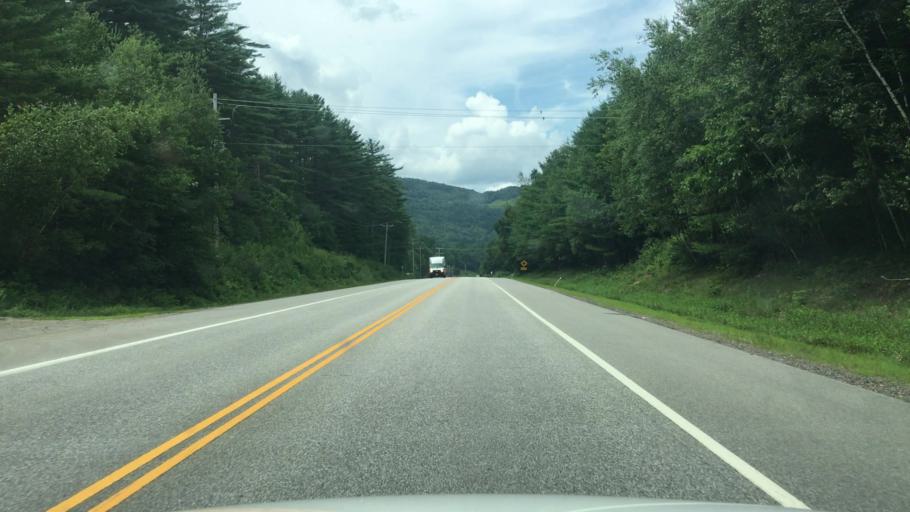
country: US
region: New Hampshire
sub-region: Grafton County
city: Rumney
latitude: 43.7948
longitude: -71.8335
